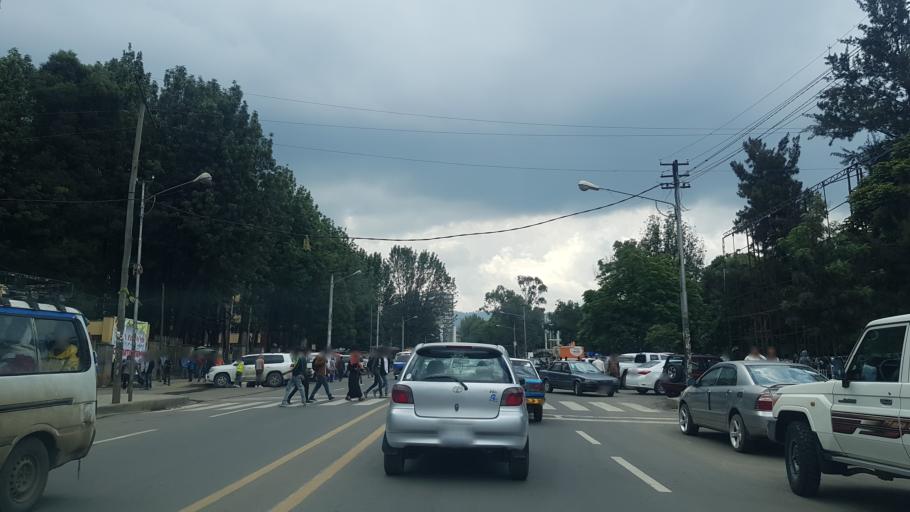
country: ET
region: Adis Abeba
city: Addis Ababa
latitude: 9.0397
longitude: 38.7623
